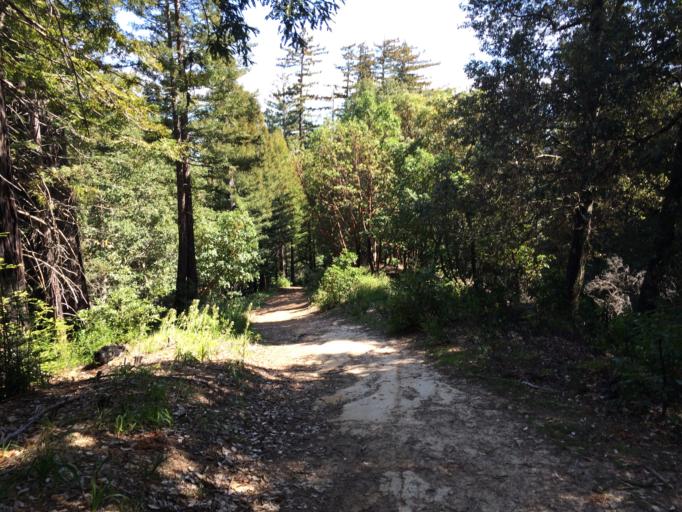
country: US
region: California
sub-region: Santa Cruz County
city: Boulder Creek
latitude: 37.2012
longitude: -122.2322
